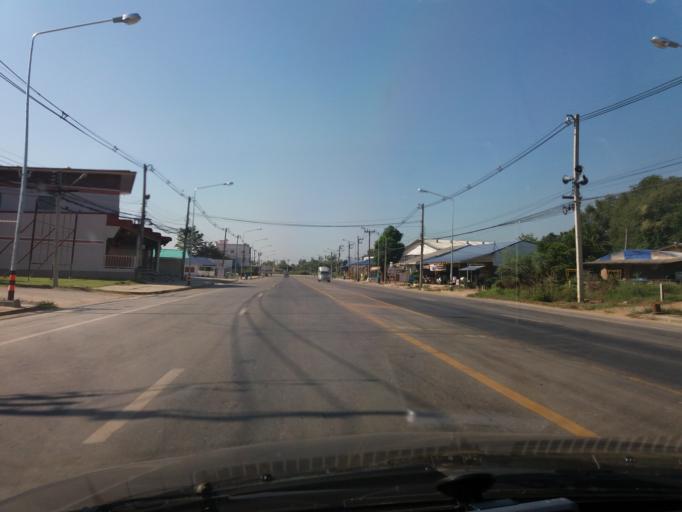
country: TH
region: Kamphaeng Phet
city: Khlong Khlung
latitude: 16.2235
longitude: 99.7293
